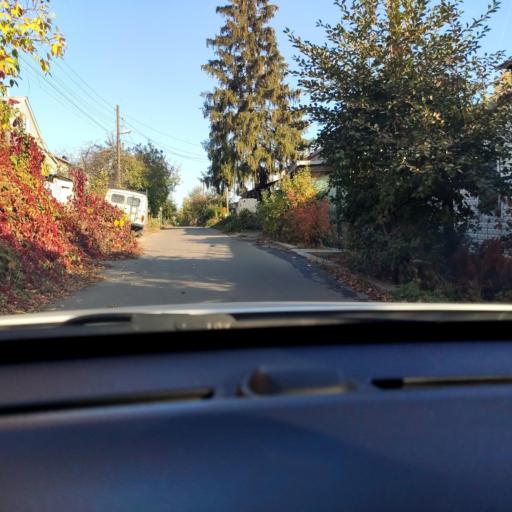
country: RU
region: Voronezj
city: Voronezh
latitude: 51.7077
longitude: 39.2386
